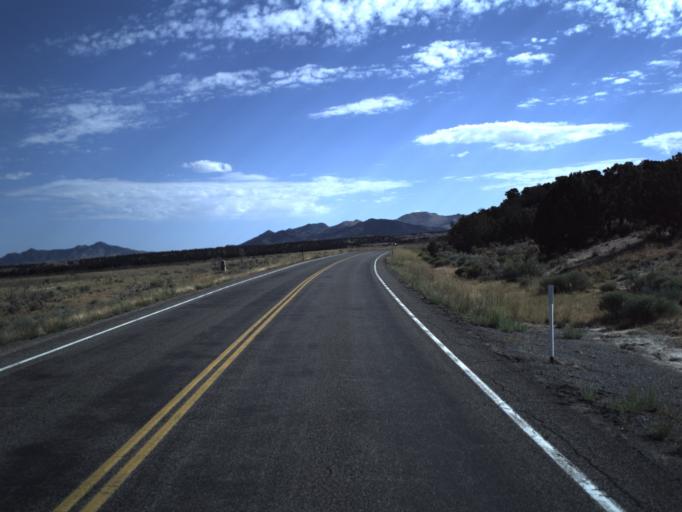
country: US
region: Utah
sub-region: Juab County
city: Mona
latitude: 39.7586
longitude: -112.1791
